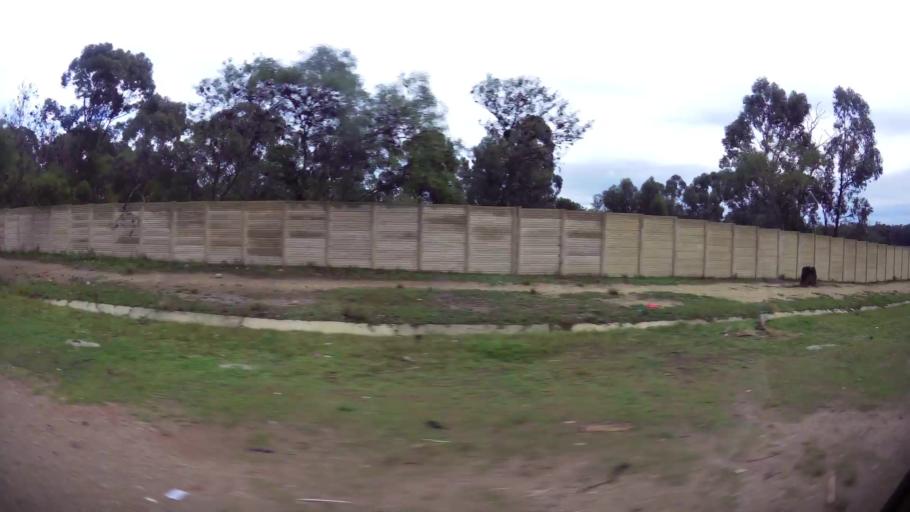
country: ZA
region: Eastern Cape
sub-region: Nelson Mandela Bay Metropolitan Municipality
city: Port Elizabeth
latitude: -33.9911
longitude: 25.5797
